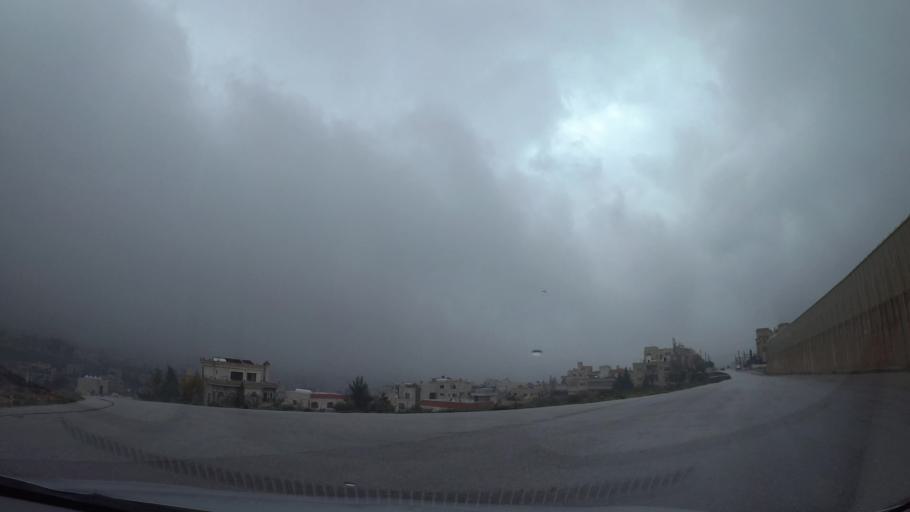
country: JO
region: Amman
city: Al Jubayhah
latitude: 32.0167
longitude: 35.8303
